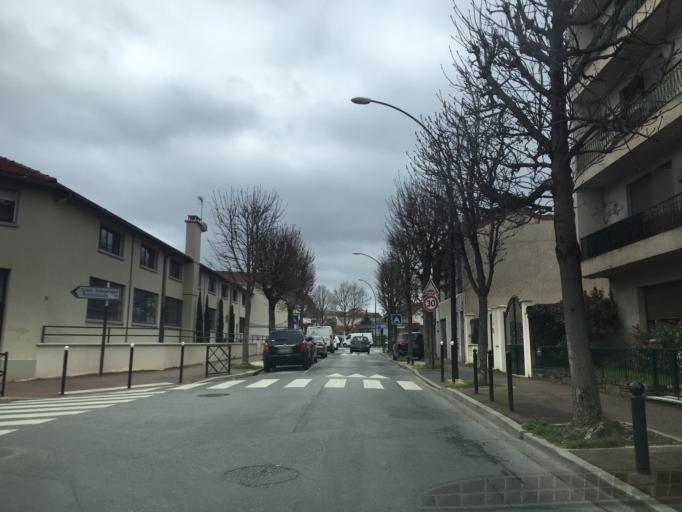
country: FR
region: Ile-de-France
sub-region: Departement du Val-de-Marne
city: Saint-Maur-des-Fosses
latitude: 48.7897
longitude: 2.4930
